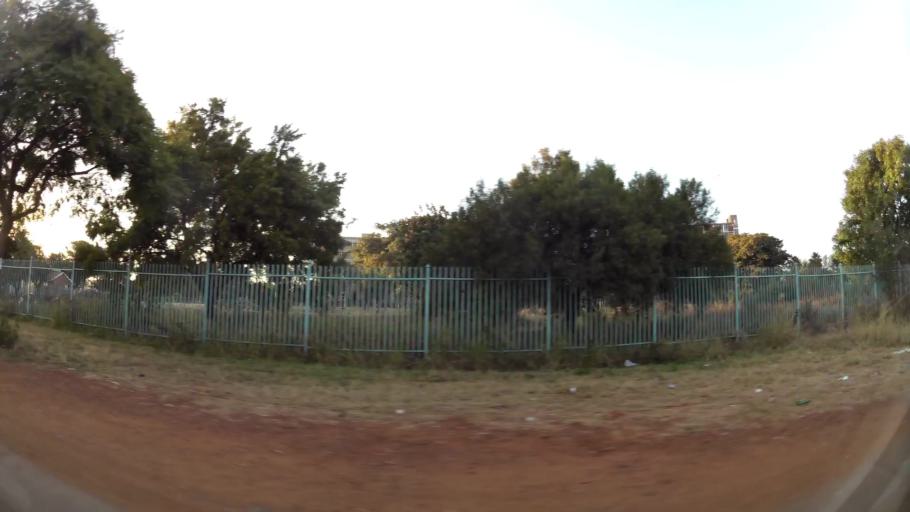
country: ZA
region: Gauteng
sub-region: City of Tshwane Metropolitan Municipality
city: Pretoria
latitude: -25.7382
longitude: 28.1400
